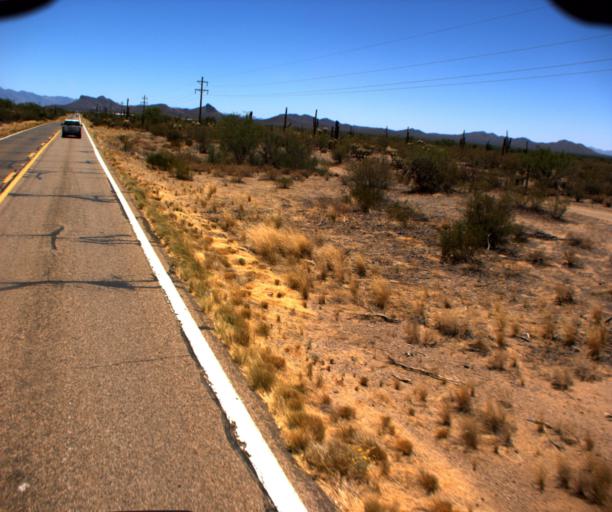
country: US
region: Arizona
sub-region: Pima County
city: Sells
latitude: 31.9435
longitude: -111.9264
